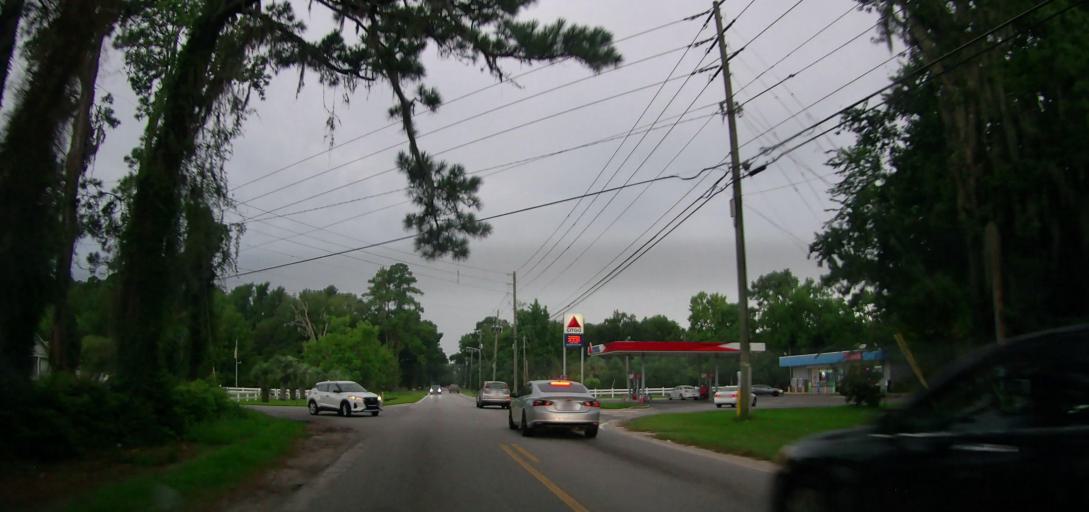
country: US
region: Georgia
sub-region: Glynn County
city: Dock Junction
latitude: 31.2247
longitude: -81.5084
